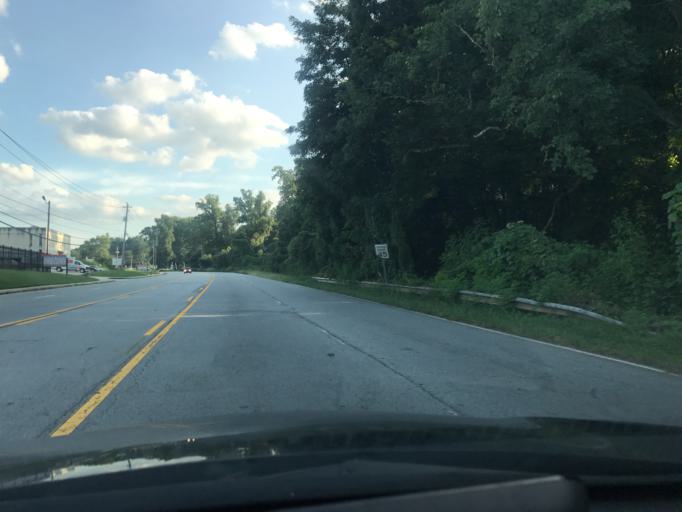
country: US
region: Georgia
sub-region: DeKalb County
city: Scottdale
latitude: 33.7888
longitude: -84.2766
